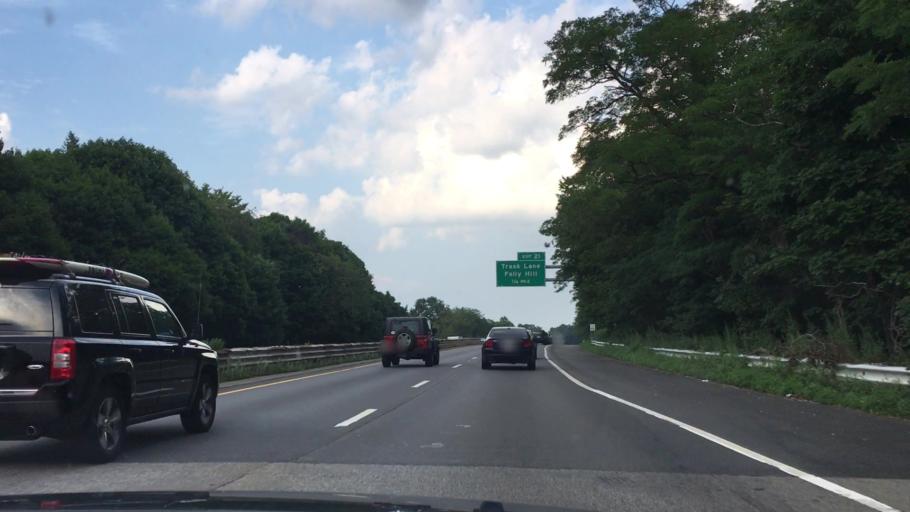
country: US
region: Massachusetts
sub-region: Essex County
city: Danvers
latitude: 42.5684
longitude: -70.9182
